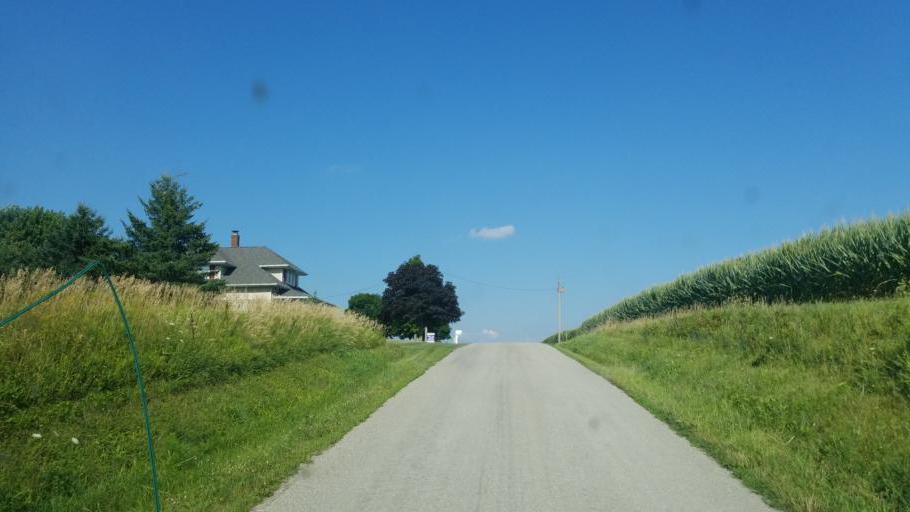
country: US
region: Ohio
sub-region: Wyandot County
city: Upper Sandusky
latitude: 40.7887
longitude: -83.3300
